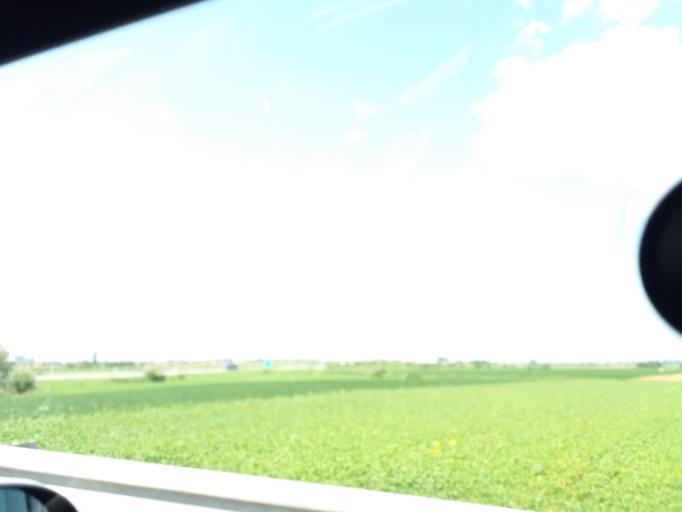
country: RS
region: Autonomna Pokrajina Vojvodina
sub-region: Sremski Okrug
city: Sremska Mitrovica
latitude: 45.0001
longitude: 19.6508
